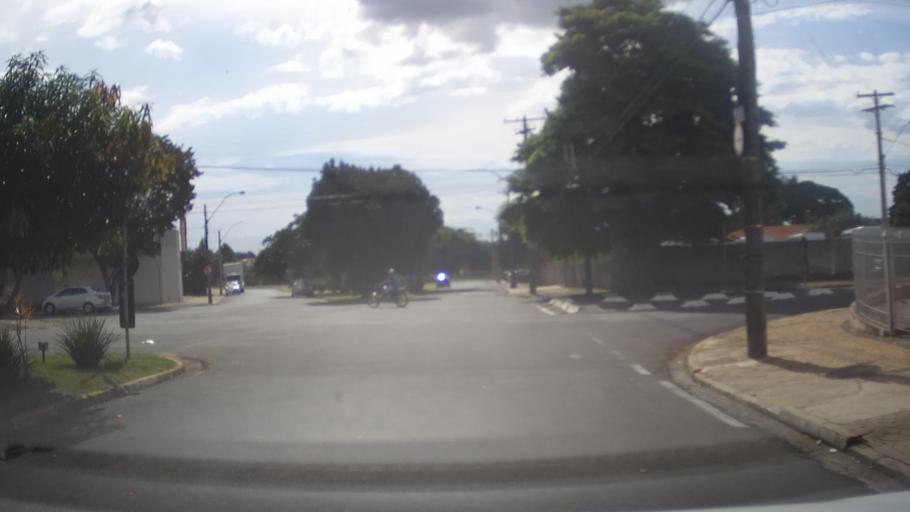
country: BR
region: Sao Paulo
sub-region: Campinas
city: Campinas
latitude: -22.8868
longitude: -47.1118
